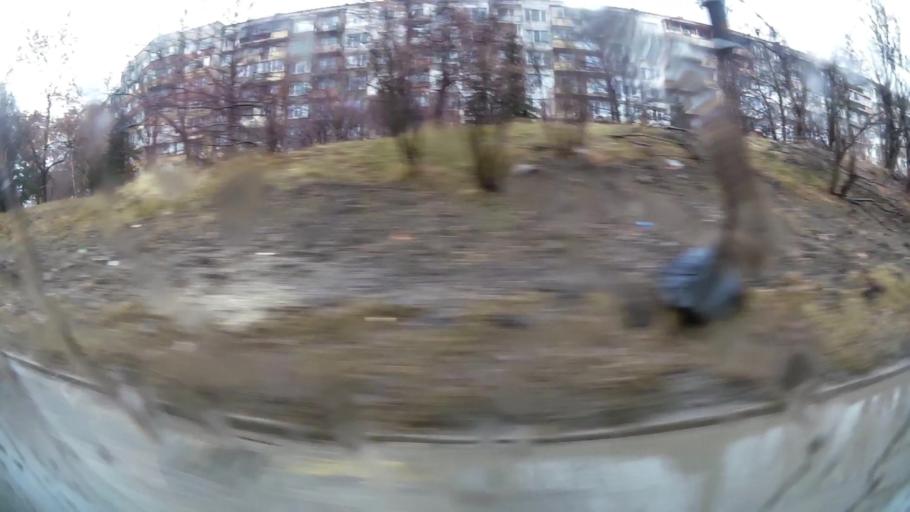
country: BG
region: Sofia-Capital
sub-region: Stolichna Obshtina
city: Sofia
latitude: 42.6492
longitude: 23.3723
